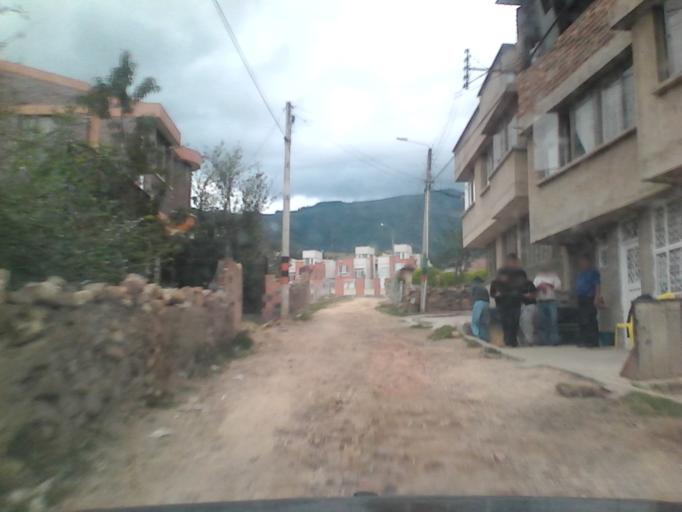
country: CO
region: Boyaca
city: Duitama
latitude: 5.8421
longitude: -73.0338
